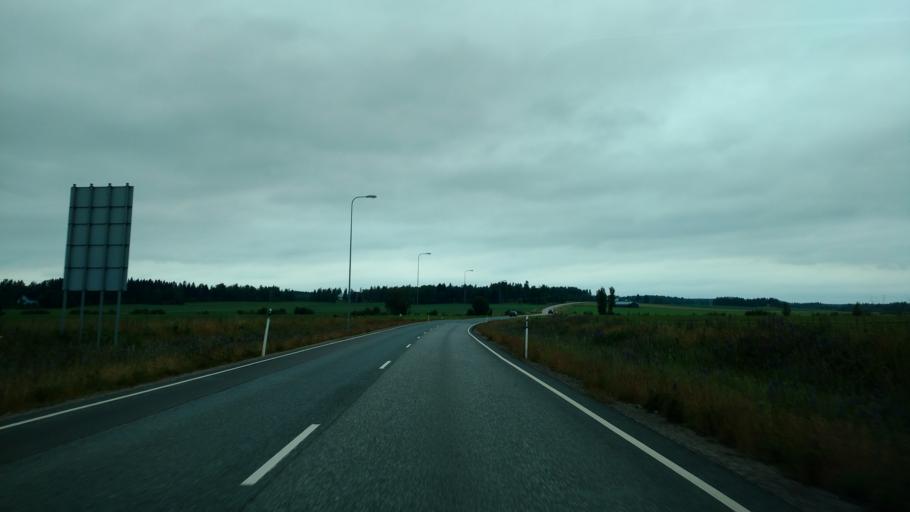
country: FI
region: Varsinais-Suomi
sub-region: Salo
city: Kiikala
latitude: 60.3930
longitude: 23.5857
